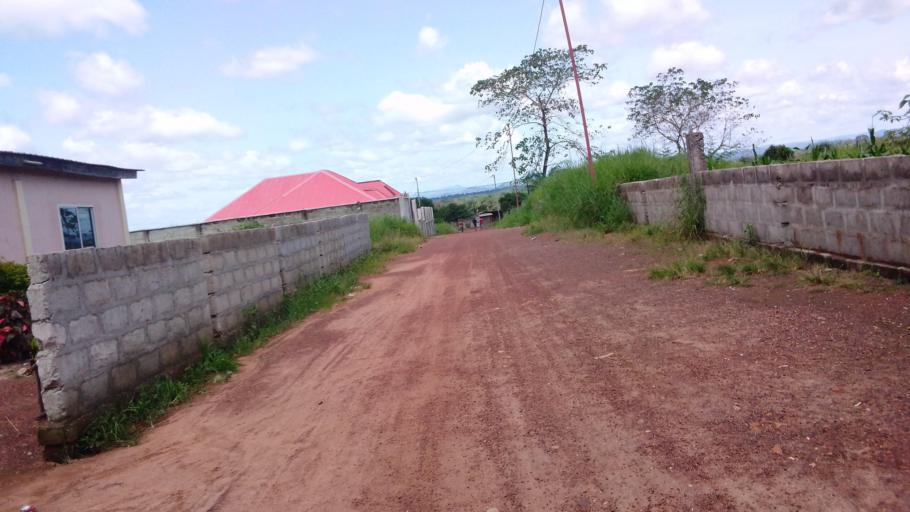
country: SL
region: Northern Province
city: Makeni
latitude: 8.8809
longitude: -12.0270
